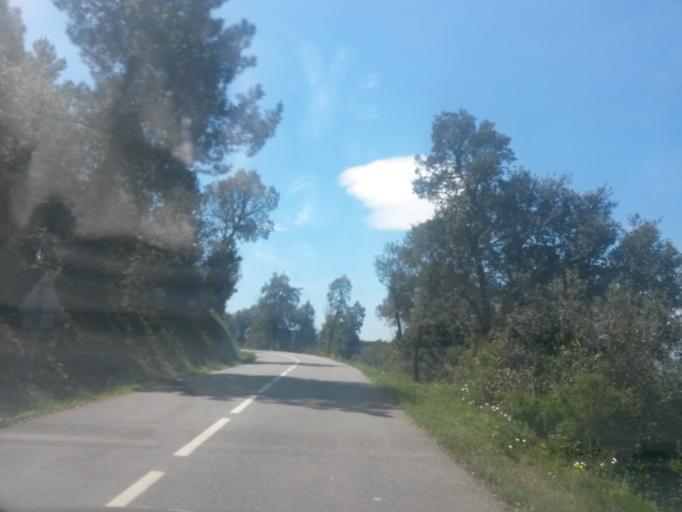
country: ES
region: Catalonia
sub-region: Provincia de Girona
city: Cassa de la Selva
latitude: 41.9141
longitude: 2.9081
